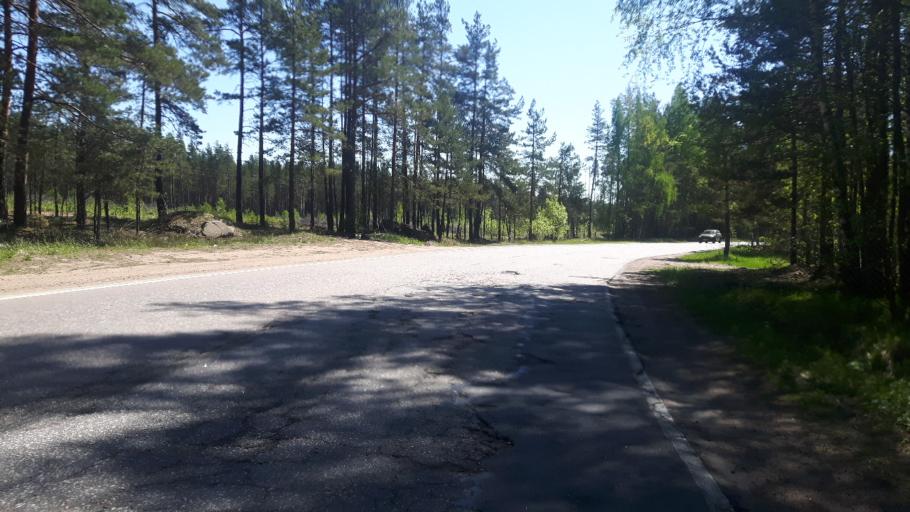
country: RU
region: Leningrad
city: Glebychevo
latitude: 60.3454
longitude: 28.8220
